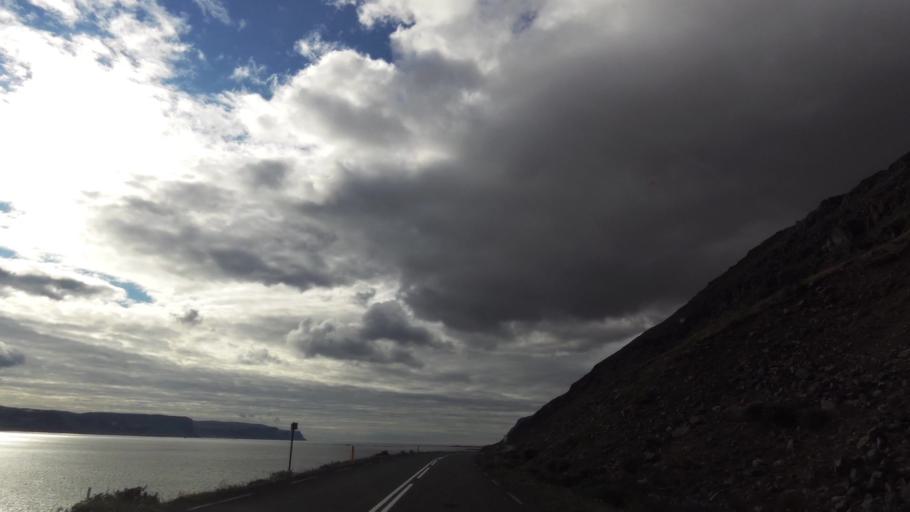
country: IS
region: West
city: Olafsvik
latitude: 65.5607
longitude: -23.9091
